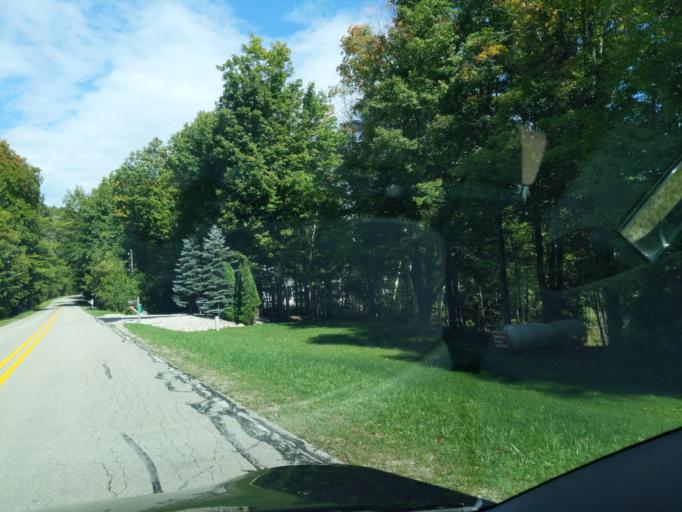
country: US
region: Michigan
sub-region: Antrim County
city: Elk Rapids
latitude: 44.9472
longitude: -85.3233
